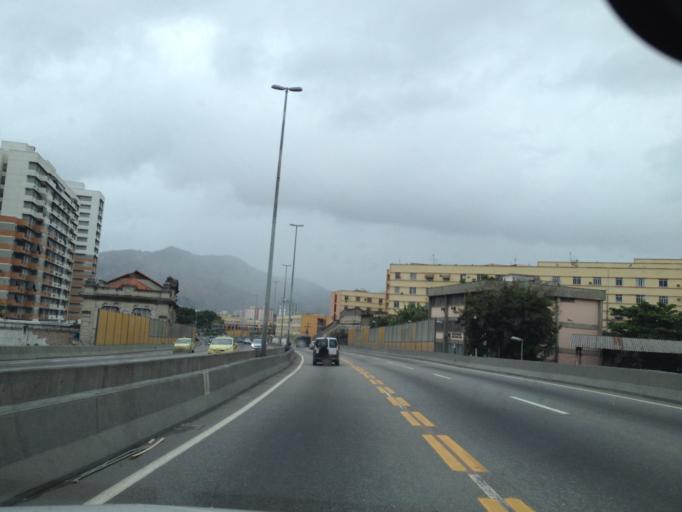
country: BR
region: Rio de Janeiro
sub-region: Rio De Janeiro
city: Rio de Janeiro
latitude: -22.8843
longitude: -43.2905
